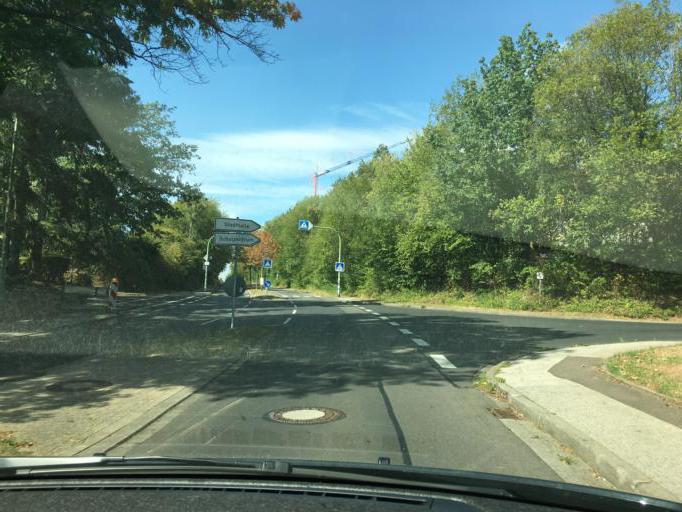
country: DE
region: North Rhine-Westphalia
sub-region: Regierungsbezirk Koln
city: Nideggen
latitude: 50.6961
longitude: 6.4790
